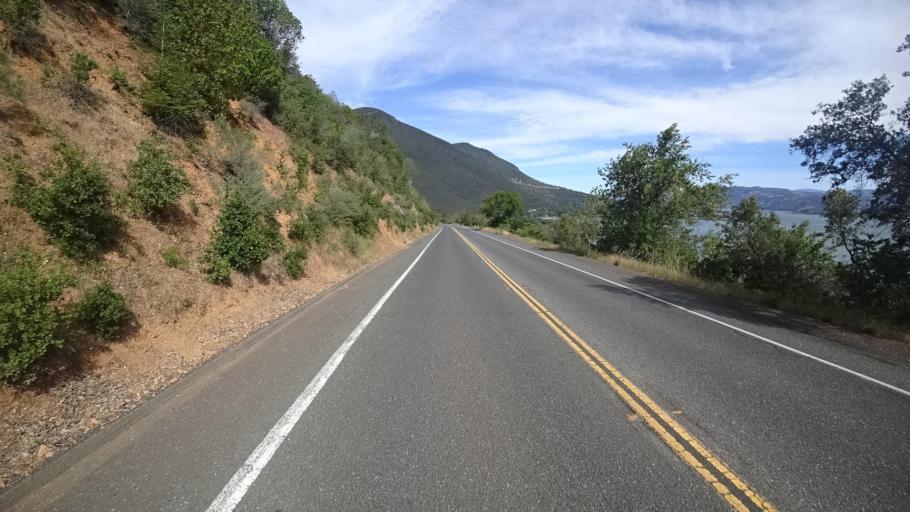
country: US
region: California
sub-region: Lake County
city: Soda Bay
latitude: 38.9612
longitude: -122.7313
